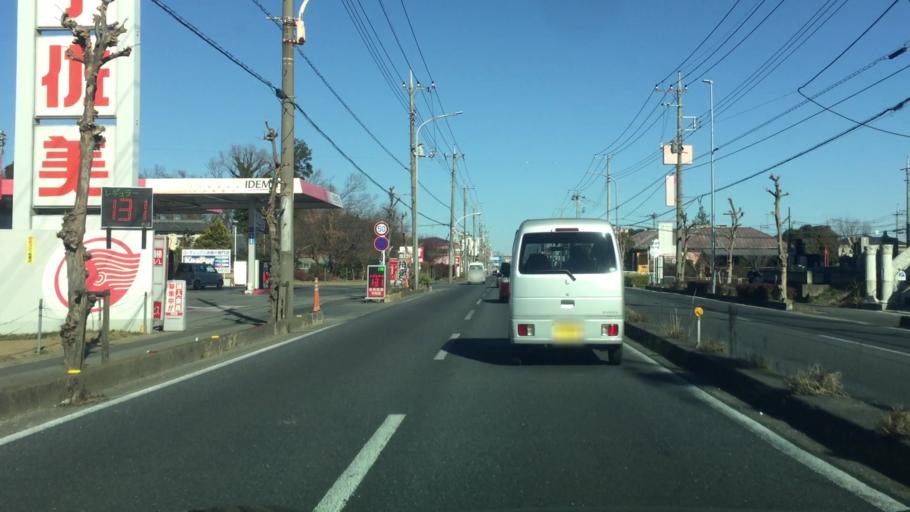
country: JP
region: Saitama
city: Hasuda
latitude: 35.9738
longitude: 139.6372
